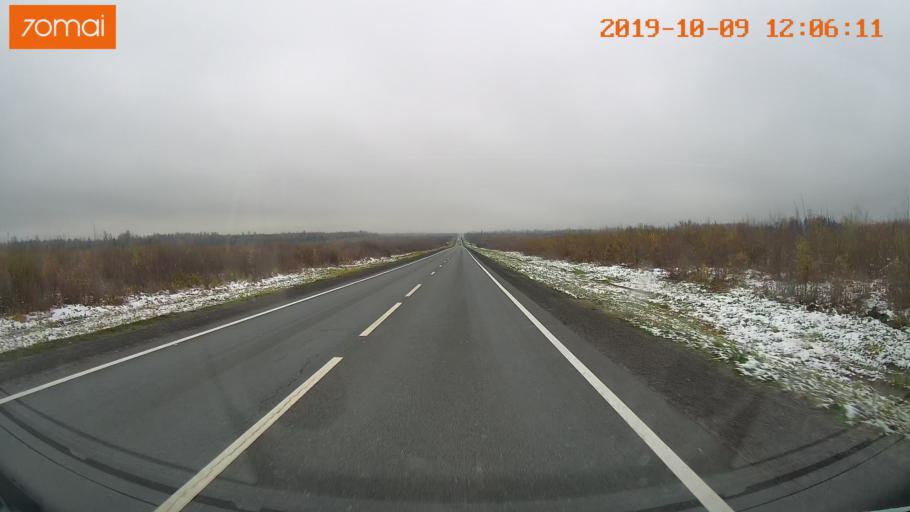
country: RU
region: Jaroslavl
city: Prechistoye
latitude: 58.6183
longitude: 40.3334
